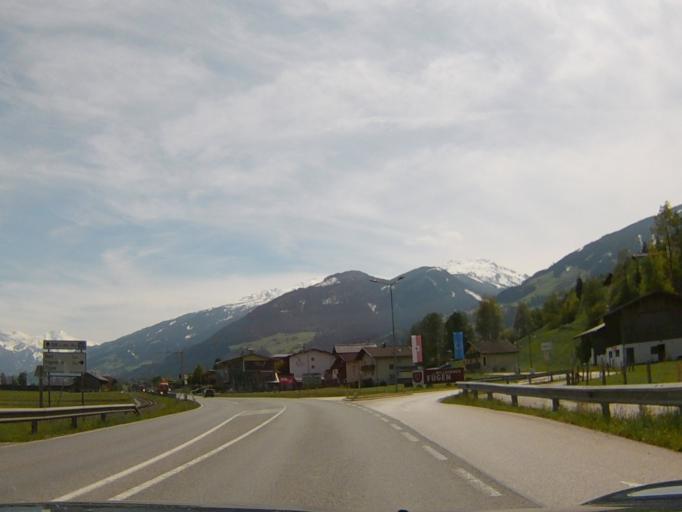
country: AT
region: Tyrol
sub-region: Politischer Bezirk Schwaz
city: Fugen
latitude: 47.3542
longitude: 11.8514
